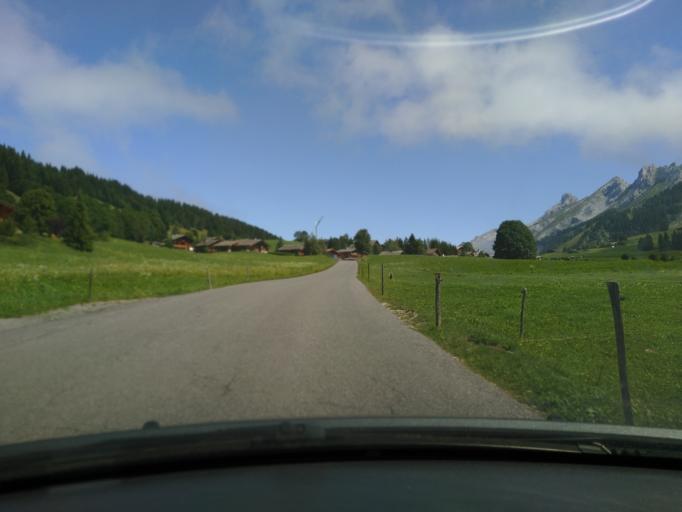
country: FR
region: Rhone-Alpes
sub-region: Departement de la Haute-Savoie
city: Le Grand-Bornand
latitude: 45.9158
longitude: 6.4720
